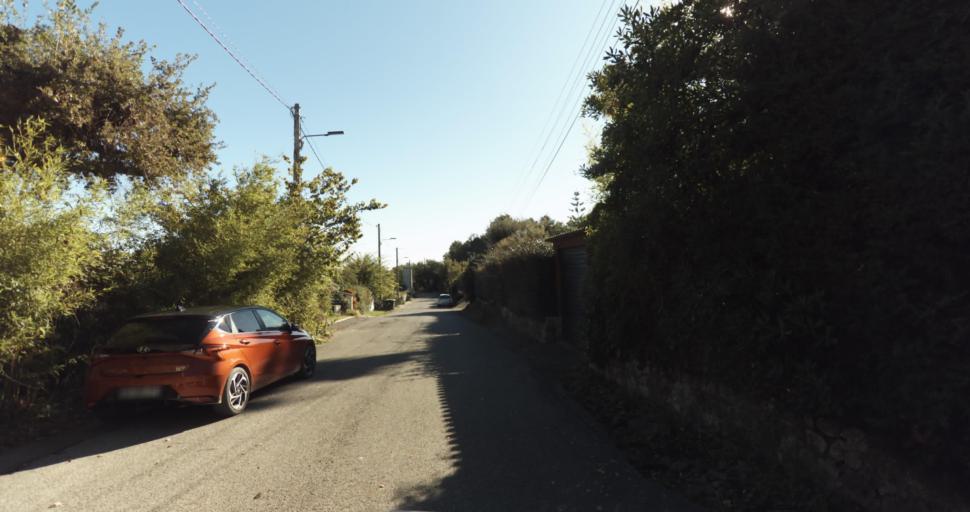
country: FR
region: Provence-Alpes-Cote d'Azur
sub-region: Departement des Alpes-Maritimes
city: Vence
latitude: 43.7166
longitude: 7.1125
